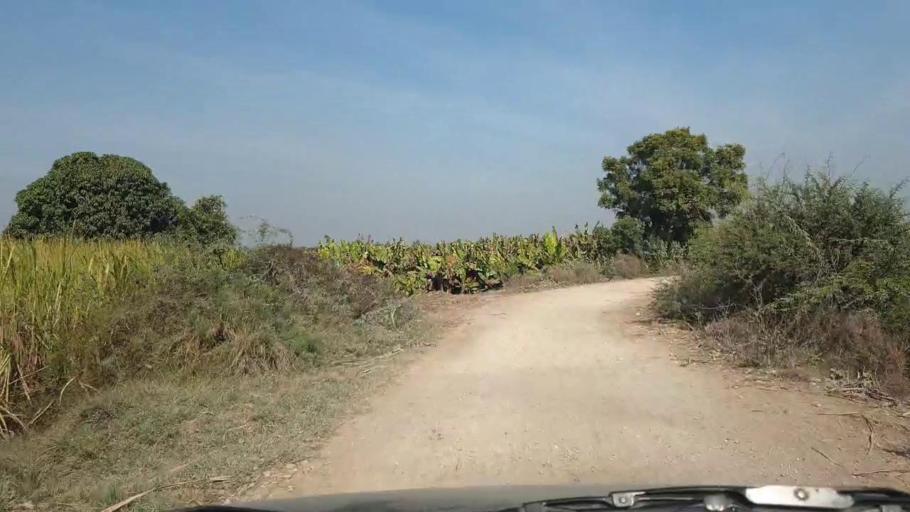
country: PK
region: Sindh
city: Tando Allahyar
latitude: 25.4049
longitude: 68.7506
